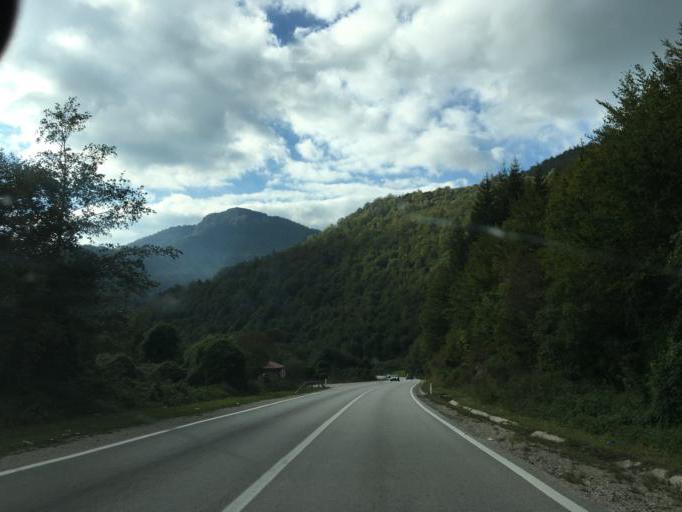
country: BA
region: Federation of Bosnia and Herzegovina
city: Bugojno
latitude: 44.0929
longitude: 17.5659
